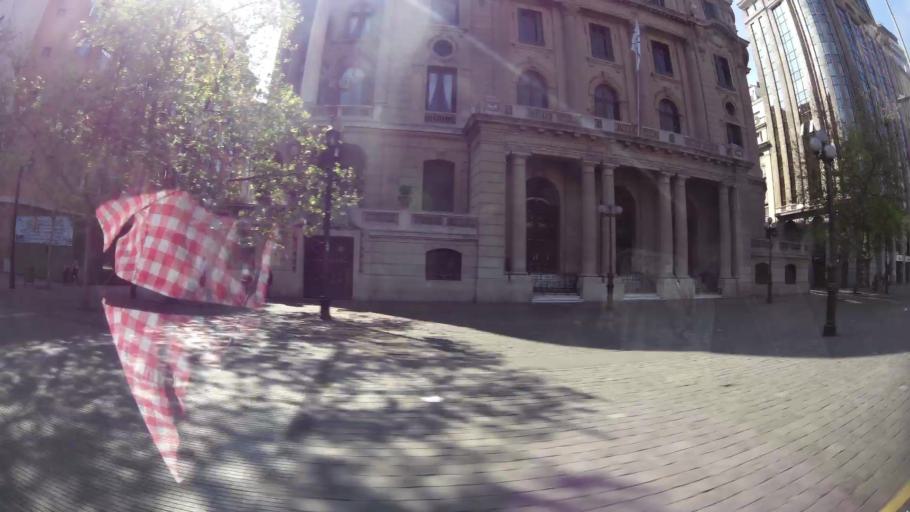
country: CL
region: Santiago Metropolitan
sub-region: Provincia de Santiago
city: Santiago
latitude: -33.4438
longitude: -70.6515
